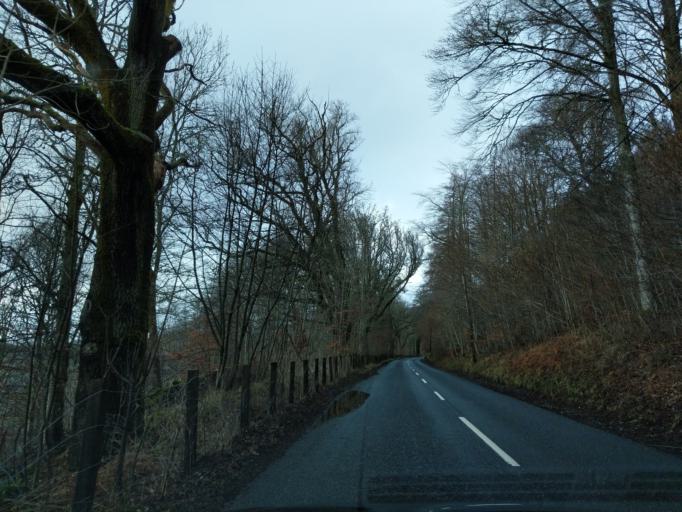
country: GB
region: Scotland
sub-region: Perth and Kinross
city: Aberfeldy
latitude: 56.5752
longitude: -4.0565
